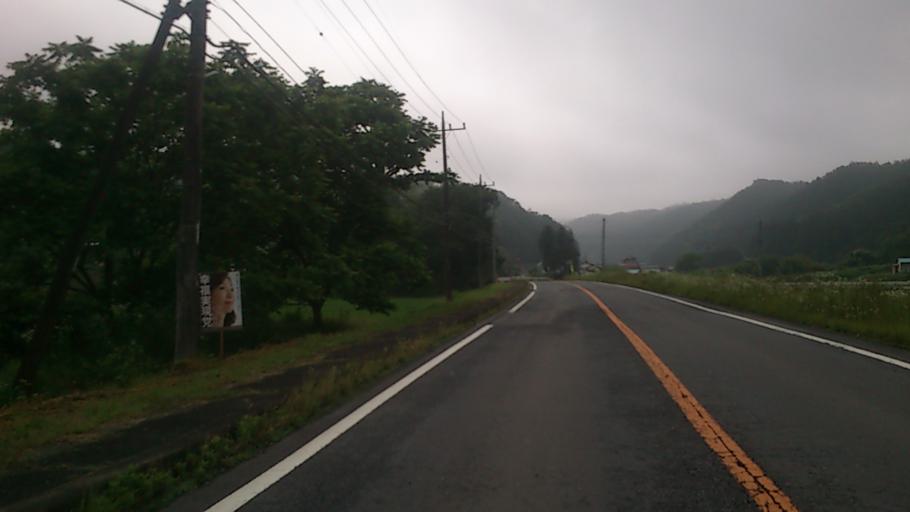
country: JP
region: Tochigi
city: Karasuyama
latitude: 36.6582
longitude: 140.2551
